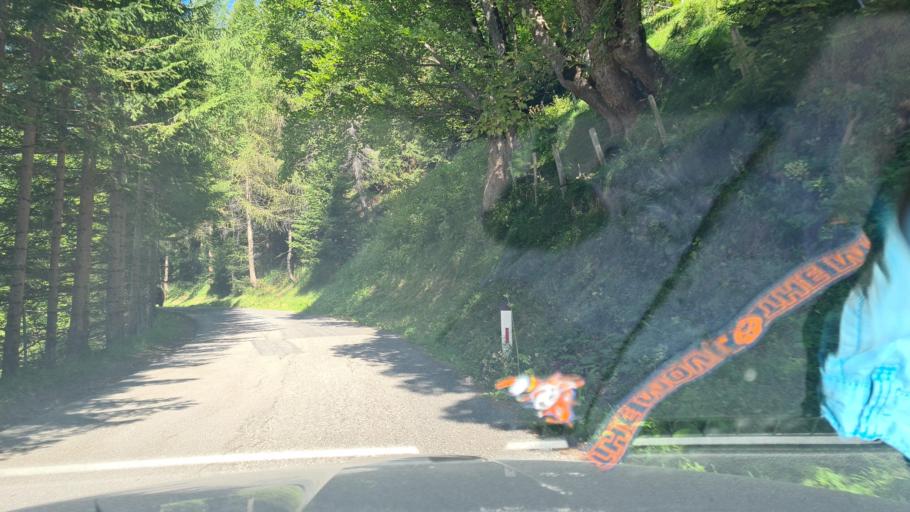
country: AT
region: Salzburg
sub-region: Politischer Bezirk Tamsweg
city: Zederhaus
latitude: 47.1843
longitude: 13.4354
